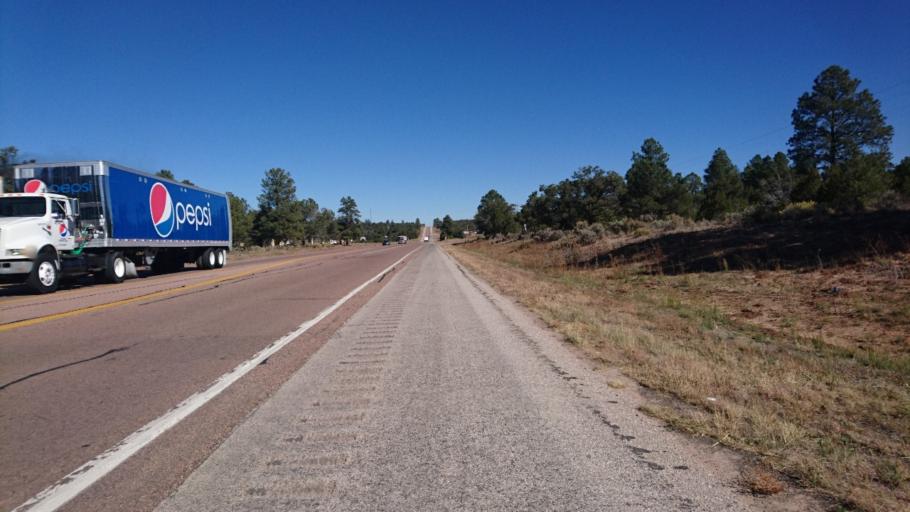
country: US
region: New Mexico
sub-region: McKinley County
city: Black Rock
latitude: 35.2336
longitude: -108.7651
